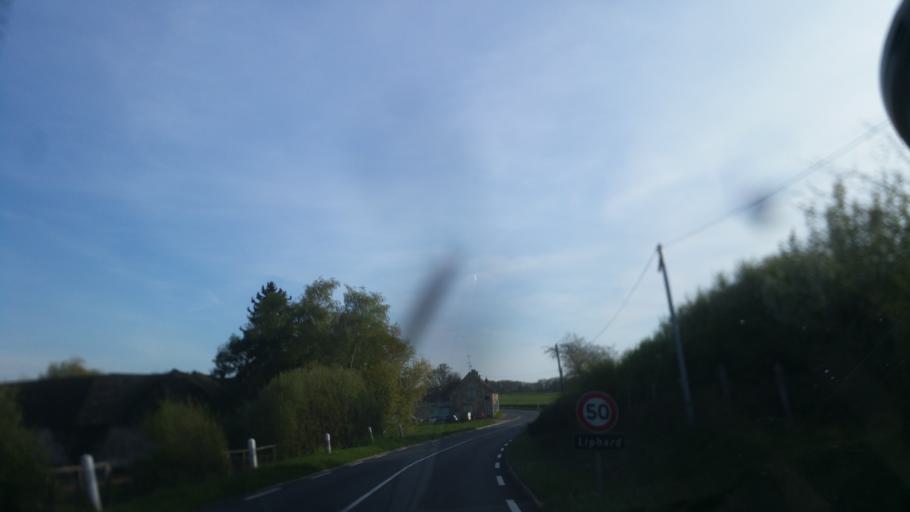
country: FR
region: Ile-de-France
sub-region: Departement de l'Essonne
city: Dourdan
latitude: 48.5457
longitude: 2.0195
